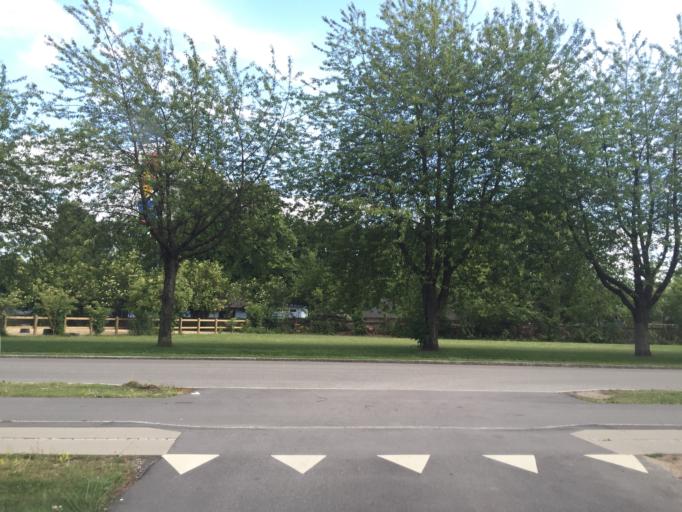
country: DK
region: Capital Region
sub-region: Rodovre Kommune
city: Rodovre
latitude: 55.6688
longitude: 12.4438
